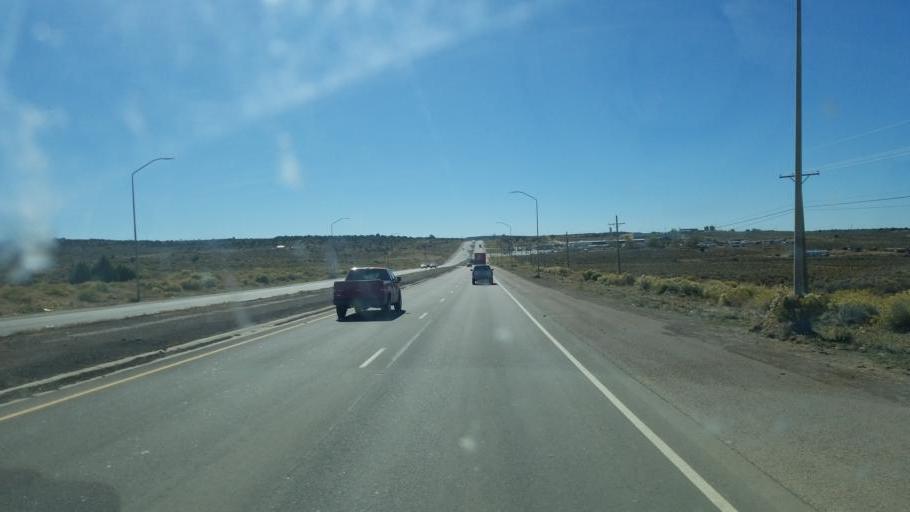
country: US
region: New Mexico
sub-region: McKinley County
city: Gallup
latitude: 35.6142
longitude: -108.7784
